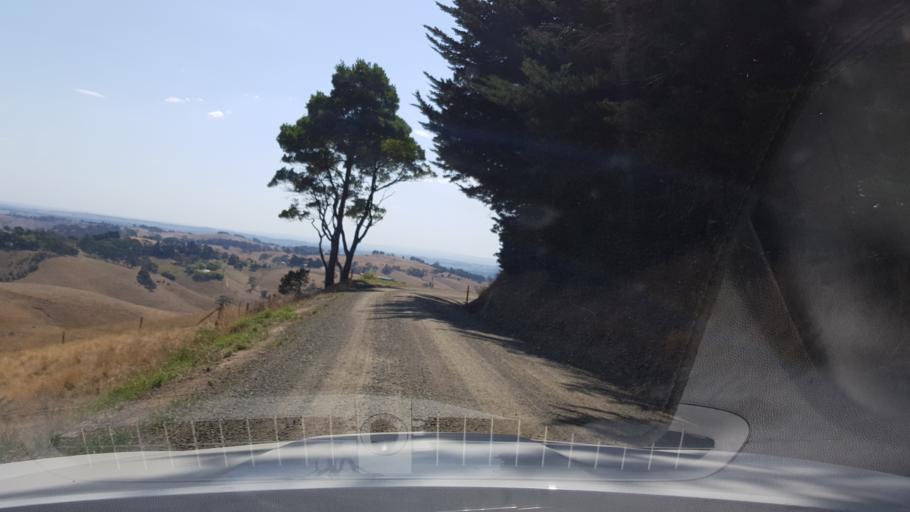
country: AU
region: Victoria
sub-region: Baw Baw
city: Warragul
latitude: -38.2920
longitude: 145.9159
